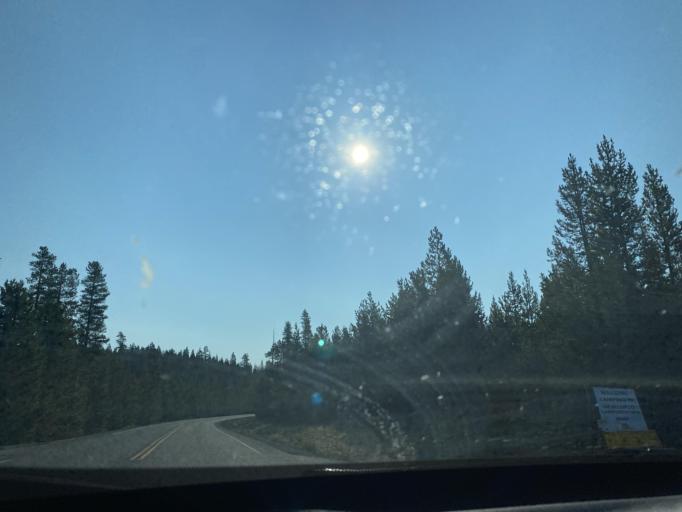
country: US
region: Oregon
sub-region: Deschutes County
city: Three Rivers
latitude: 43.7060
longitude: -121.2988
